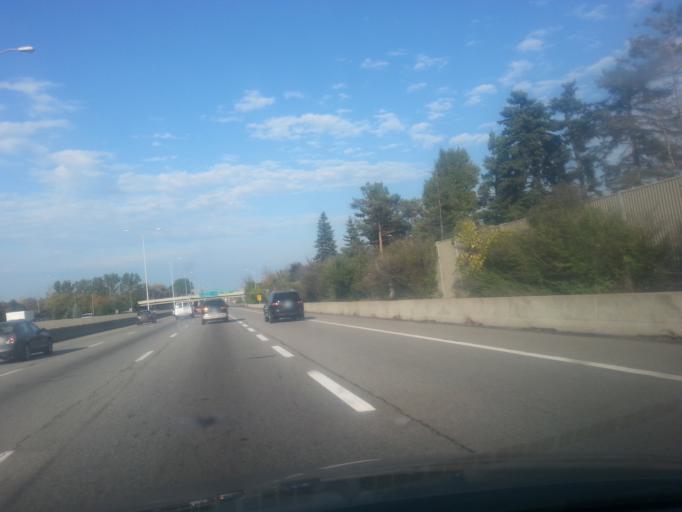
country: CA
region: Ontario
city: Ottawa
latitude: 45.3680
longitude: -75.7569
